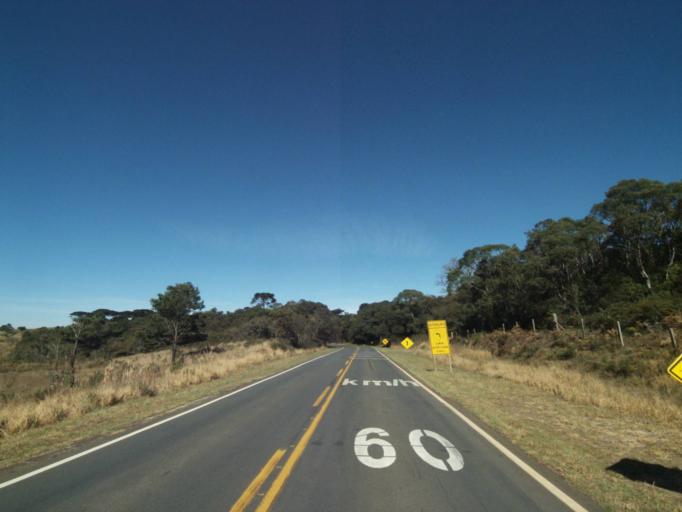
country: BR
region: Parana
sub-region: Castro
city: Castro
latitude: -24.7269
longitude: -50.1854
